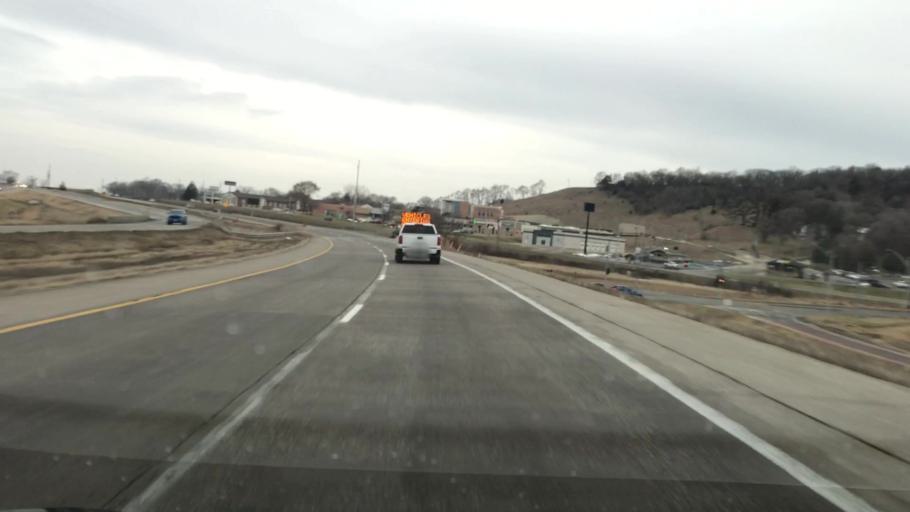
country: US
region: Iowa
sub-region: Pottawattamie County
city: Council Bluffs
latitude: 41.2432
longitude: -95.8230
